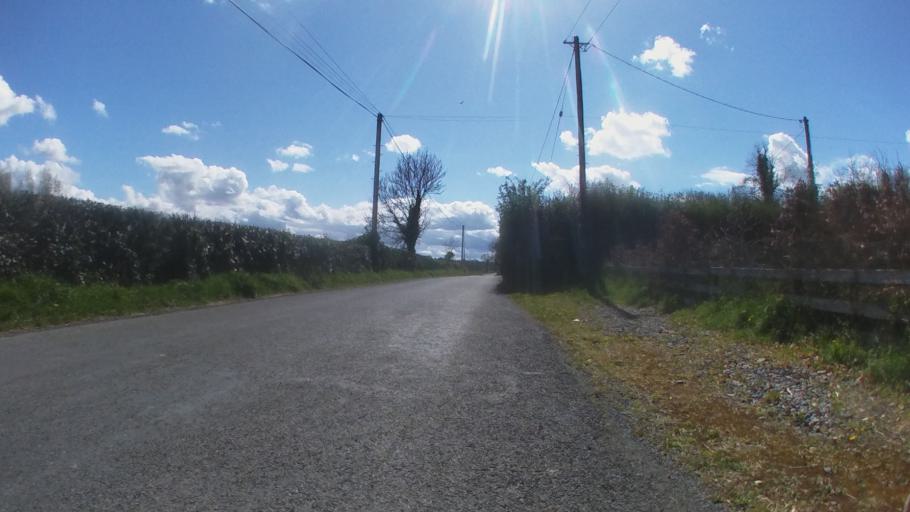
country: IE
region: Leinster
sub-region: Kilkenny
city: Thomastown
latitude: 52.5873
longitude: -7.1856
